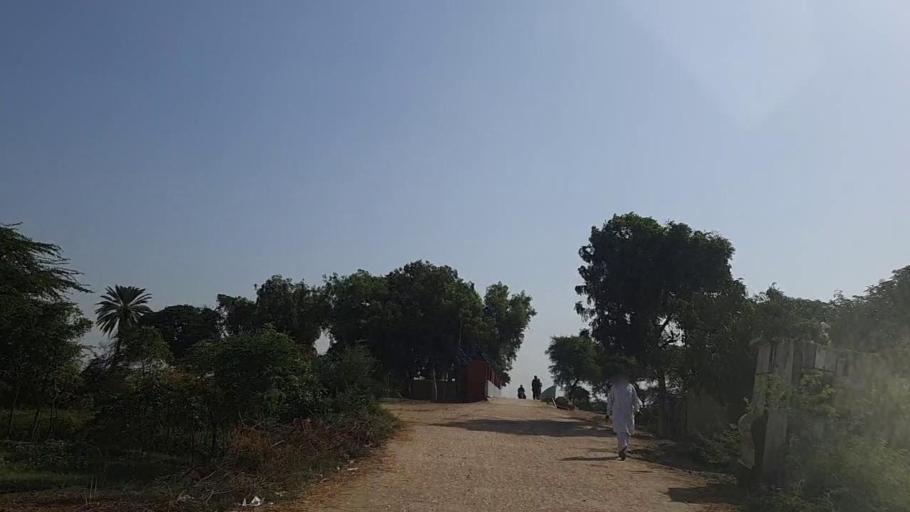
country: PK
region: Sindh
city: Daro Mehar
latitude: 24.7219
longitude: 68.0743
